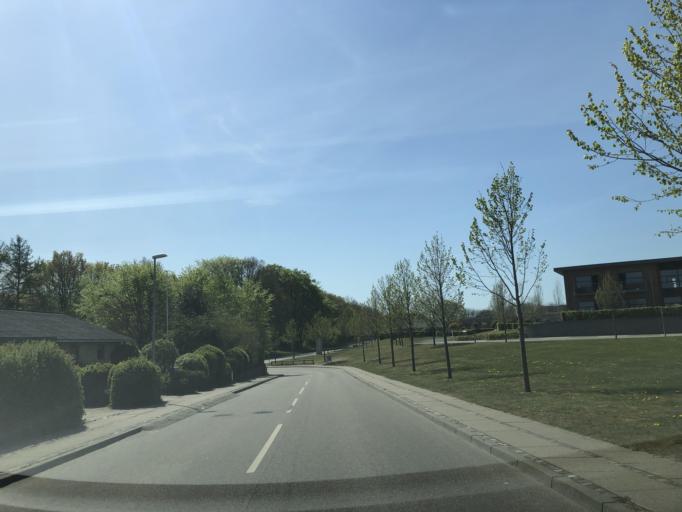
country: DK
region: North Denmark
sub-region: Mariagerfjord Kommune
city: Mariager
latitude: 56.6467
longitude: 9.9707
